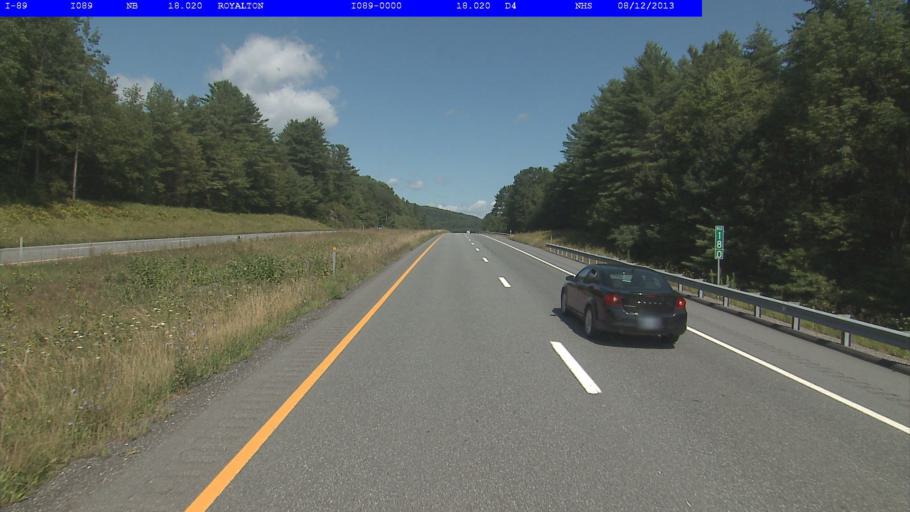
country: US
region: Vermont
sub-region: Orange County
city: Randolph
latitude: 43.8138
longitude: -72.5222
